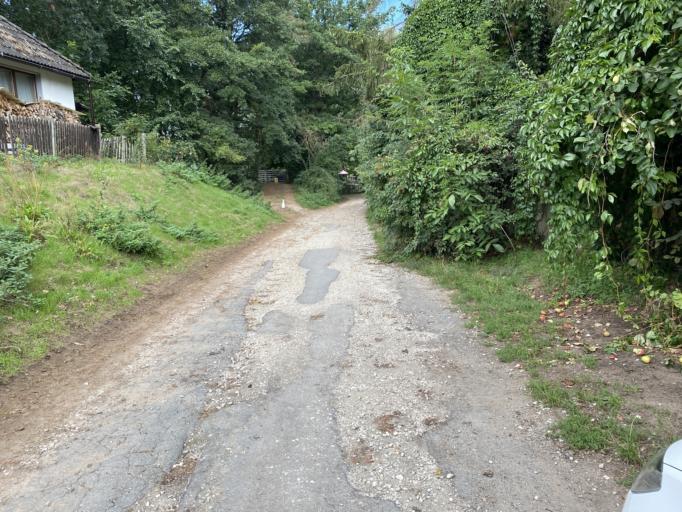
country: DE
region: Bavaria
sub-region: Regierungsbezirk Mittelfranken
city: Furth
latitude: 49.5285
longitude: 10.9776
